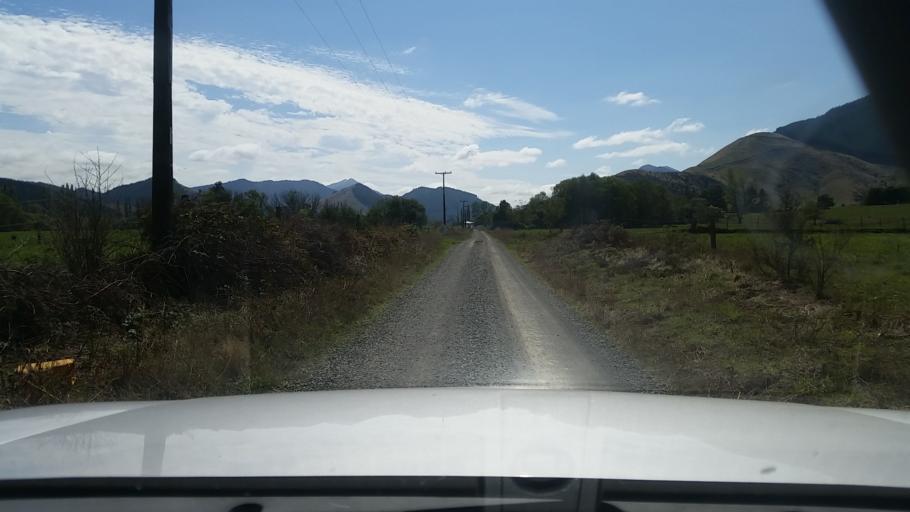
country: NZ
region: Nelson
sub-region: Nelson City
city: Nelson
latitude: -41.2558
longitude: 173.5822
